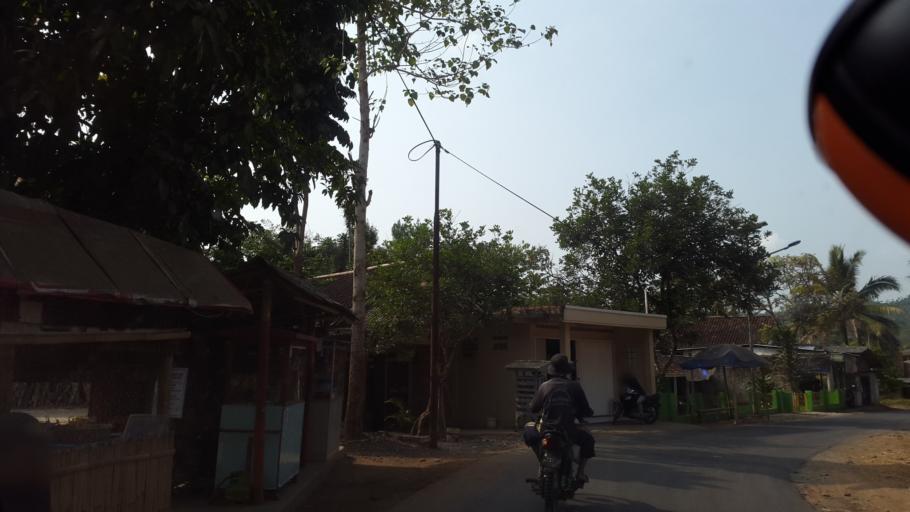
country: ID
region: West Java
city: Citampian
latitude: -7.1574
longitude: 106.7614
